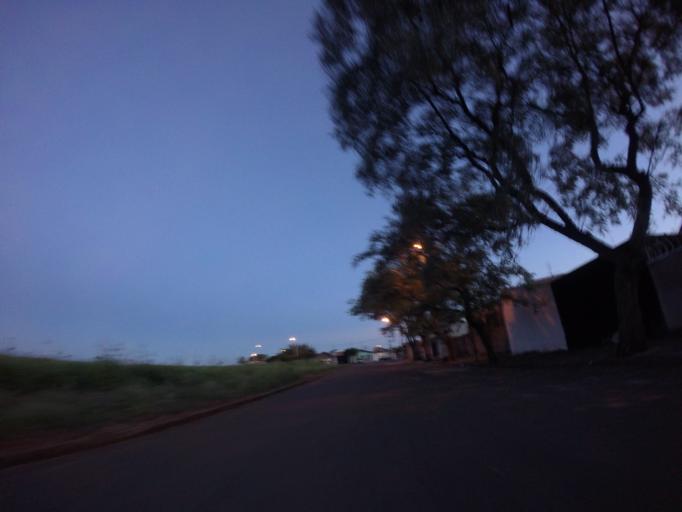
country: BR
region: Sao Paulo
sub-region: Piracicaba
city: Piracicaba
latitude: -22.7643
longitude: -47.5891
